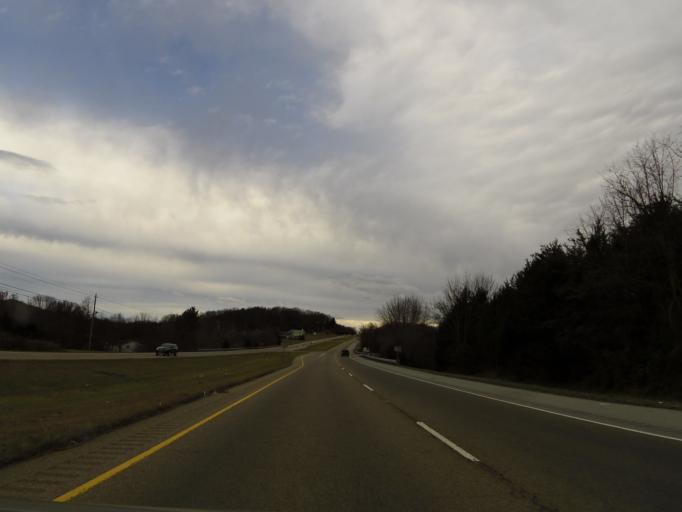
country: US
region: Tennessee
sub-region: Greene County
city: Tusculum
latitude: 36.2169
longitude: -82.7067
